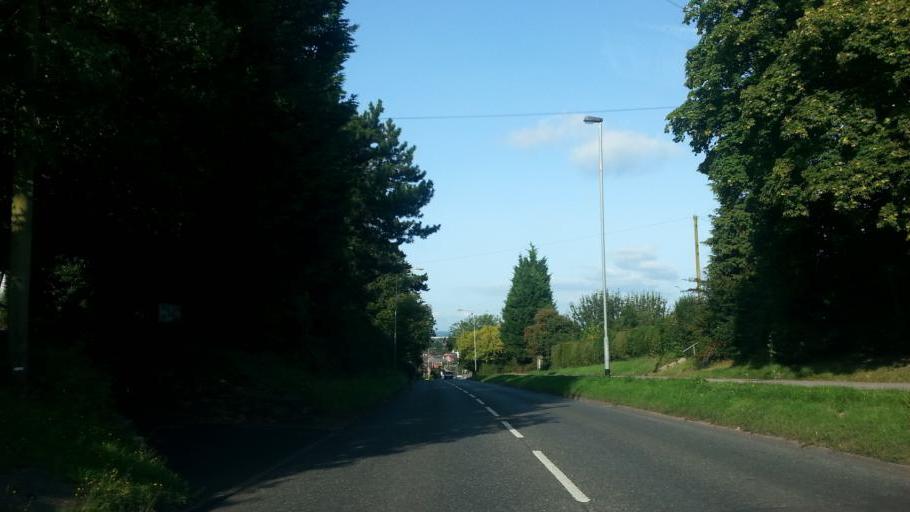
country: GB
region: England
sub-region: Nottinghamshire
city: Newark on Trent
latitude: 53.0766
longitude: -0.7866
